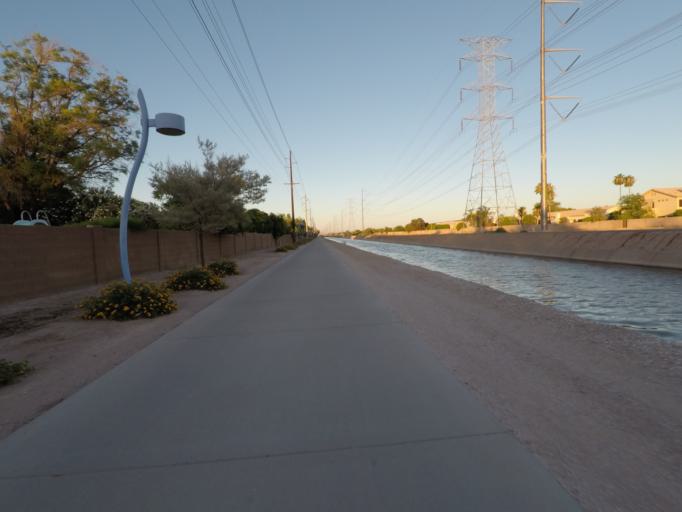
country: US
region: Arizona
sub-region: Maricopa County
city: San Carlos
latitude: 33.3569
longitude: -111.9059
